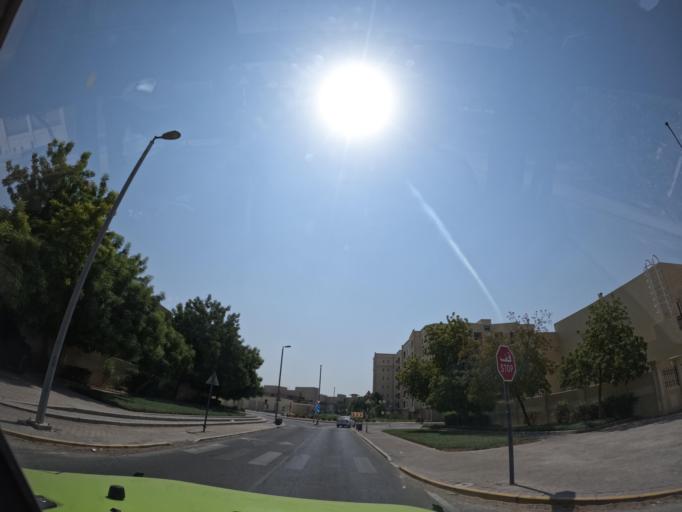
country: AE
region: Abu Dhabi
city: Abu Dhabi
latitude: 24.3146
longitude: 54.6226
